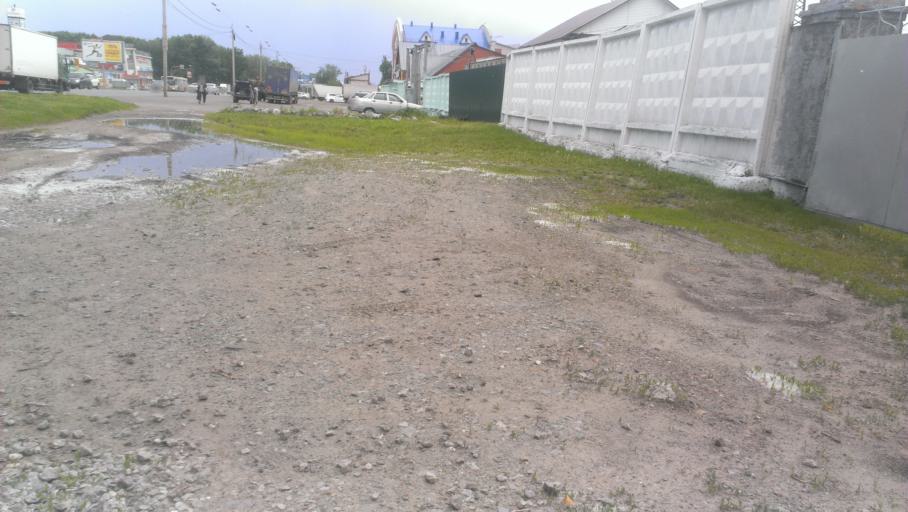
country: RU
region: Altai Krai
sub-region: Gorod Barnaulskiy
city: Barnaul
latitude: 53.3406
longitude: 83.7166
